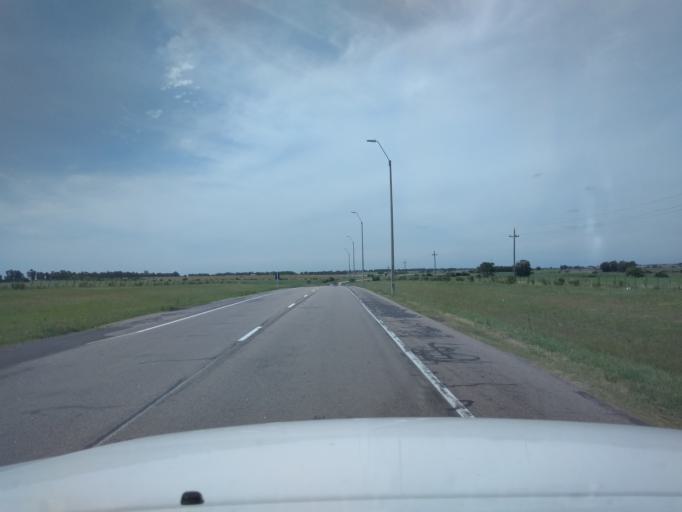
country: UY
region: Florida
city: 25 de Mayo
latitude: -34.2374
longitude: -56.2131
